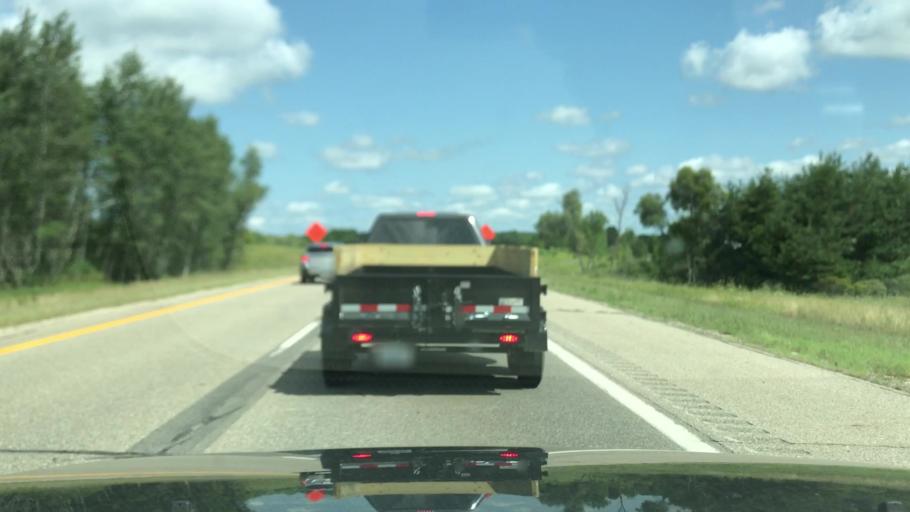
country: US
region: Michigan
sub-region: Mecosta County
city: Big Rapids
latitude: 43.7257
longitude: -85.5322
